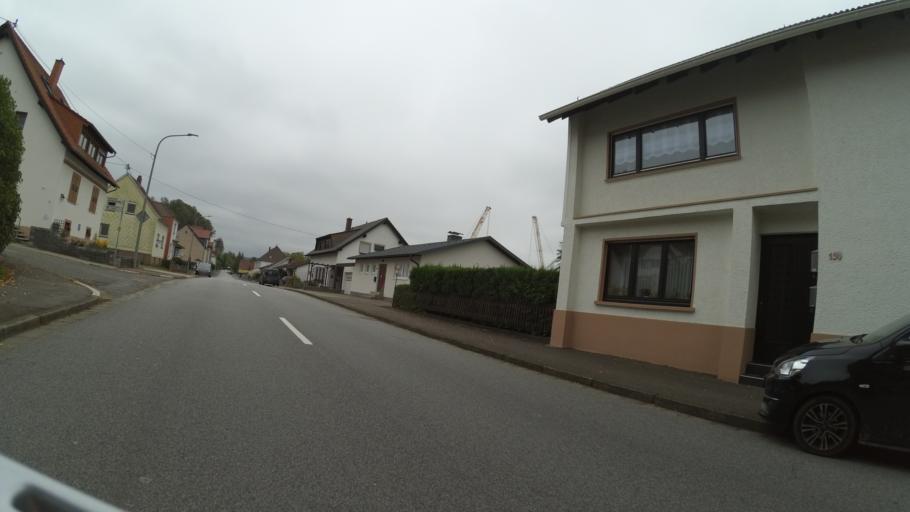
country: DE
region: Saarland
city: Blieskastel
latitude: 49.2651
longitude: 7.2904
